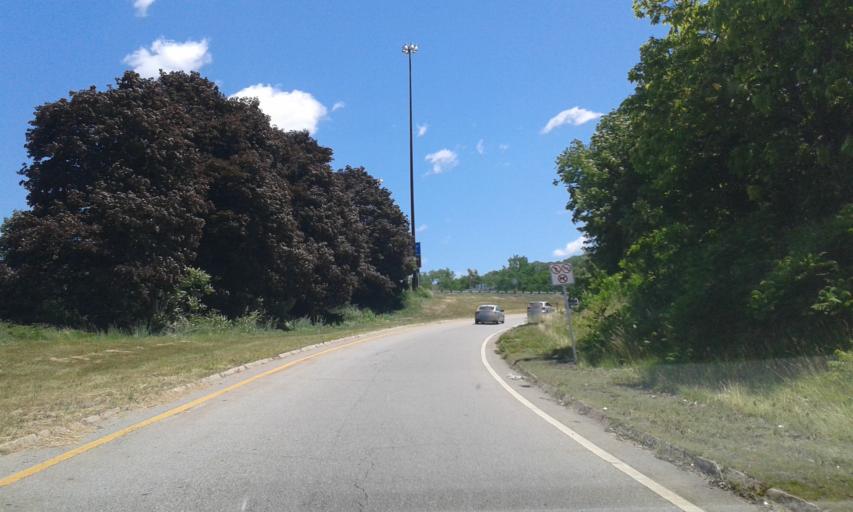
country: US
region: Massachusetts
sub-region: Middlesex County
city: Stoneham
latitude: 42.4797
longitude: -71.1165
